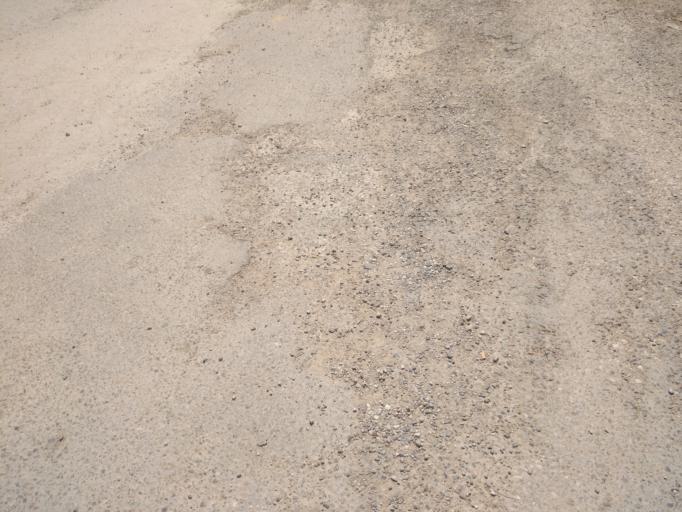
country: TN
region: Silyanah
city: Siliana
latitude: 36.0865
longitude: 9.3744
